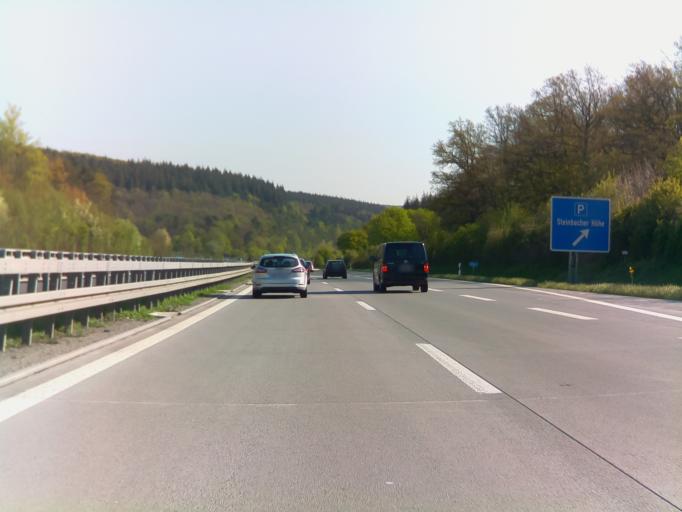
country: DE
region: Baden-Wuerttemberg
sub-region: Regierungsbezirk Stuttgart
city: Tauberbischofsheim
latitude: 49.5878
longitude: 9.6664
